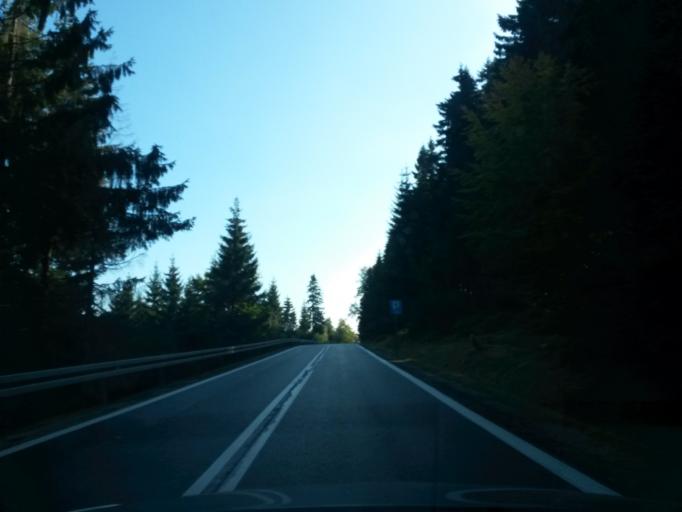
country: CZ
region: Liberecky
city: Harrachov
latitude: 50.8263
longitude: 15.4555
